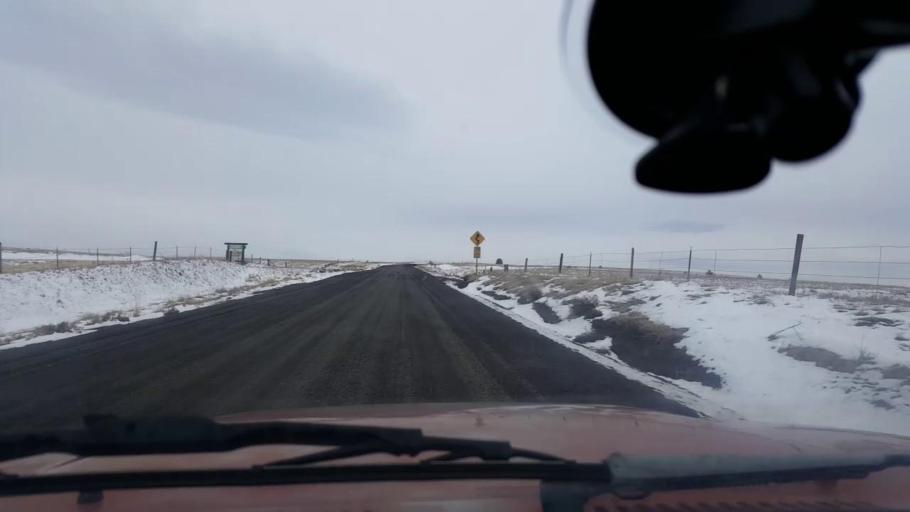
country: US
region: Washington
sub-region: Garfield County
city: Pomeroy
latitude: 46.3174
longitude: -117.4251
